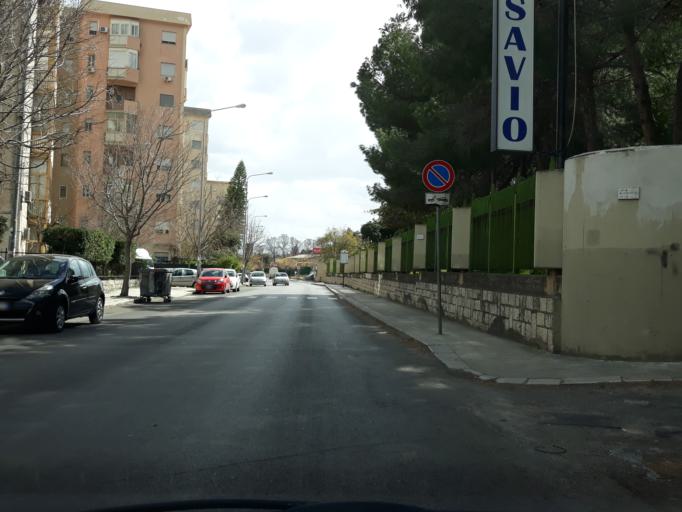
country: IT
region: Sicily
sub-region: Palermo
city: Palermo
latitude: 38.1236
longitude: 13.3193
